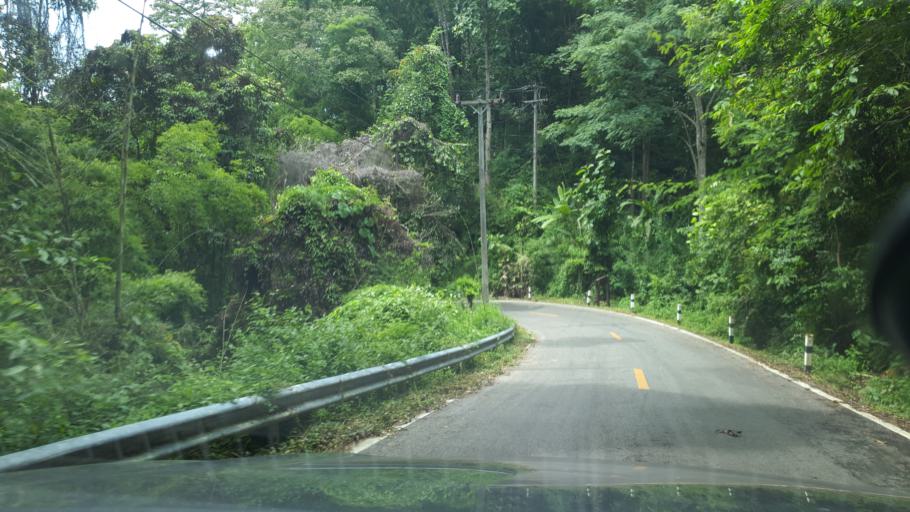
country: TH
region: Lamphun
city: Mae Tha
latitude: 18.4993
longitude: 99.2681
